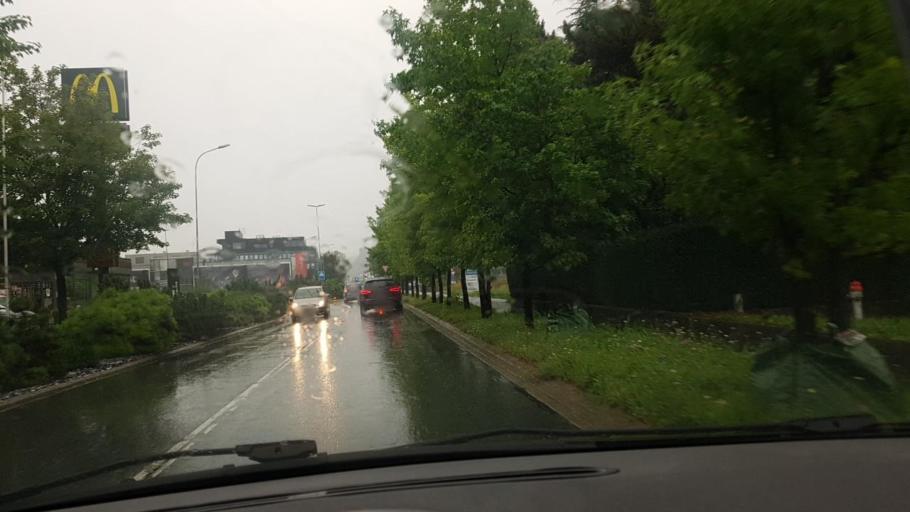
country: LI
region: Triesen
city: Triesen
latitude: 47.1188
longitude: 9.5240
